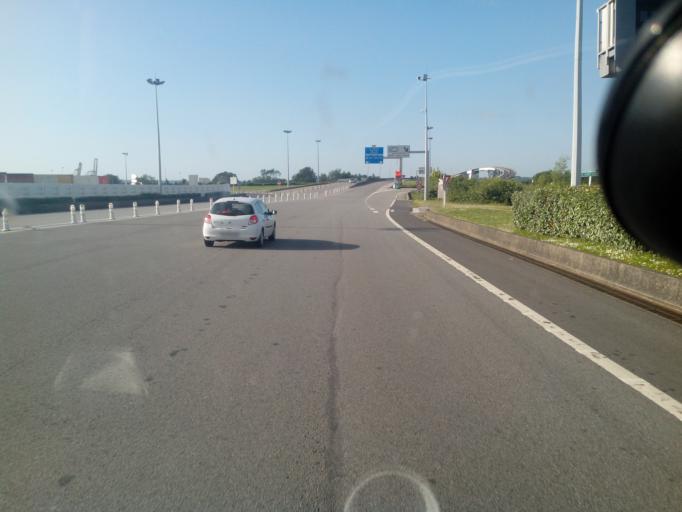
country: FR
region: Lower Normandy
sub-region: Departement du Calvados
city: La Riviere-Saint-Sauveur
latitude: 49.4512
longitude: 0.2716
